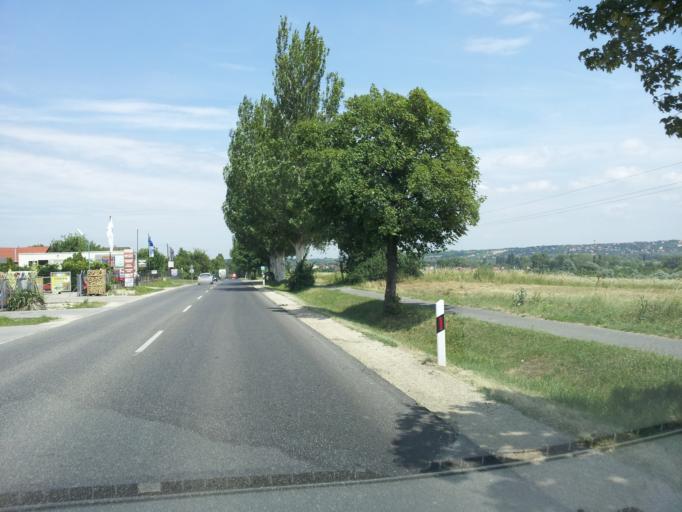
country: HU
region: Veszprem
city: Balatonalmadi
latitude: 47.0504
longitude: 18.0172
